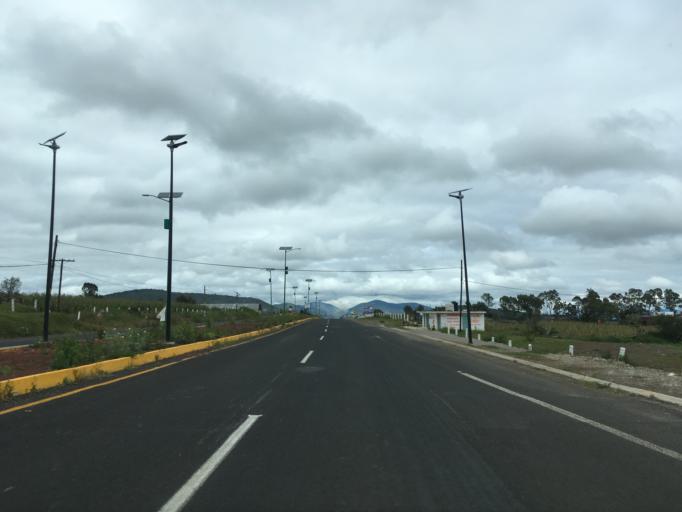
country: MX
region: Hidalgo
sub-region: Atotonilco el Grande
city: La Estancia
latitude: 20.3003
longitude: -98.6802
